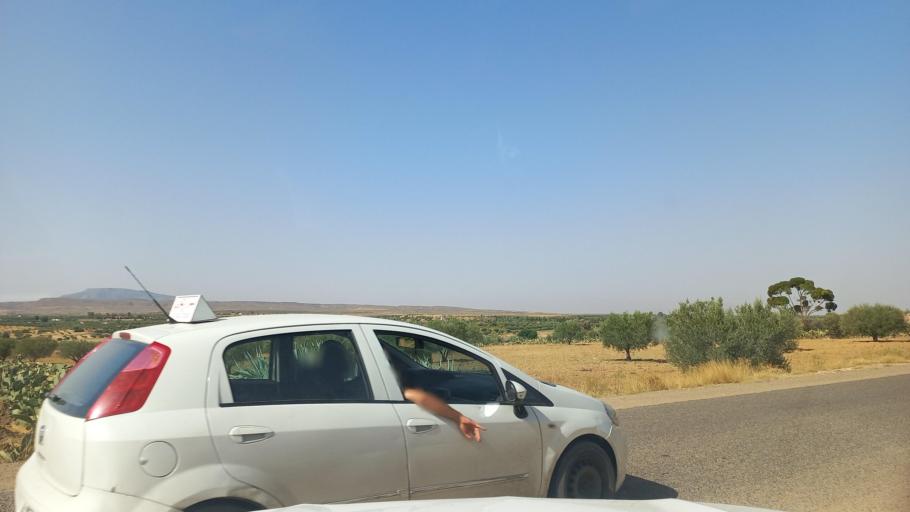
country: TN
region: Al Qasrayn
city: Kasserine
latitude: 35.2312
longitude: 9.0512
